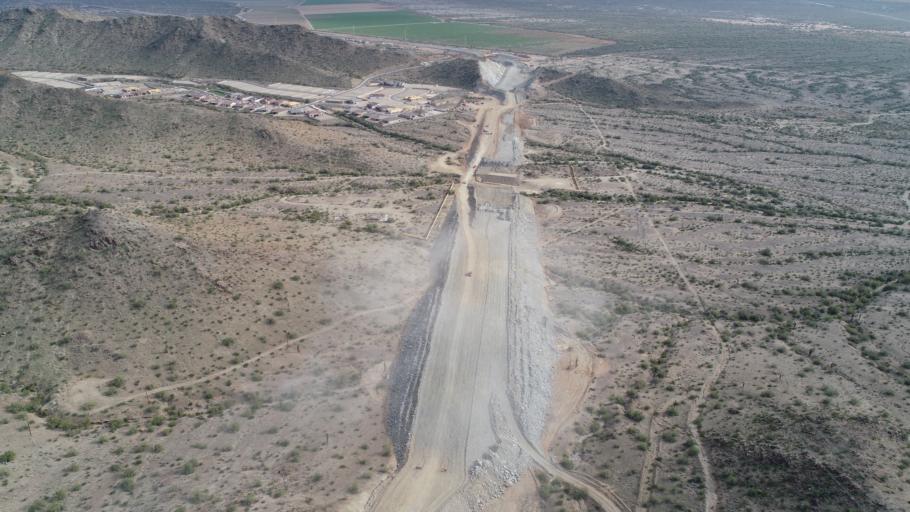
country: US
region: Arizona
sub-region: Maricopa County
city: Laveen
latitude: 33.3048
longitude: -112.1460
